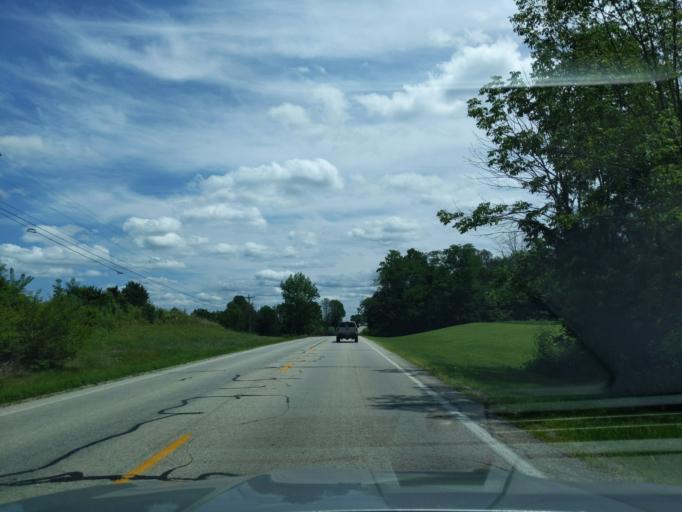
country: US
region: Indiana
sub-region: Ripley County
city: Batesville
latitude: 39.3089
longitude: -85.3006
